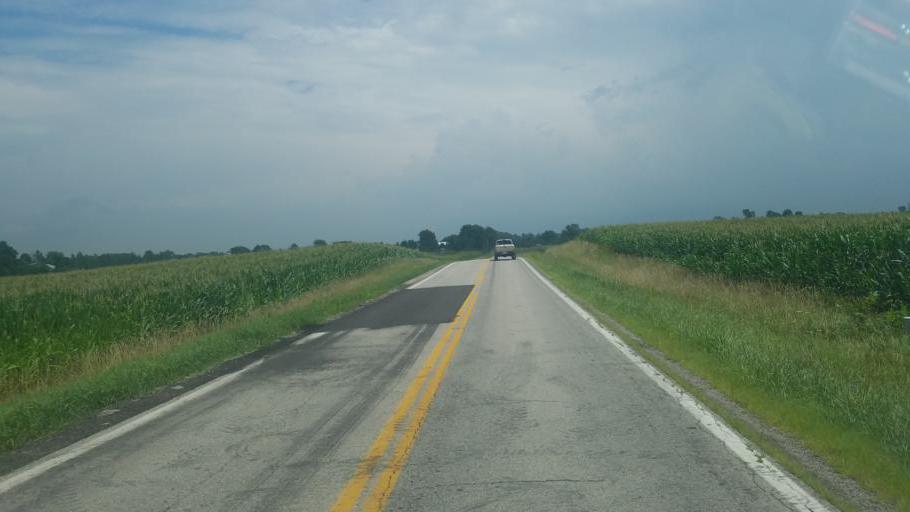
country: US
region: Ohio
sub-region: Champaign County
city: North Lewisburg
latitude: 40.4006
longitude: -83.5278
